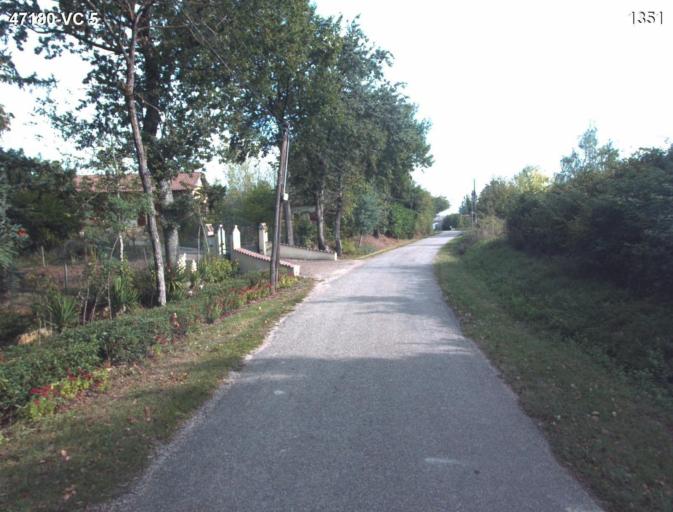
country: FR
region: Aquitaine
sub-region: Departement du Lot-et-Garonne
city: Sainte-Colombe-en-Bruilhois
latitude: 44.1714
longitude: 0.4669
